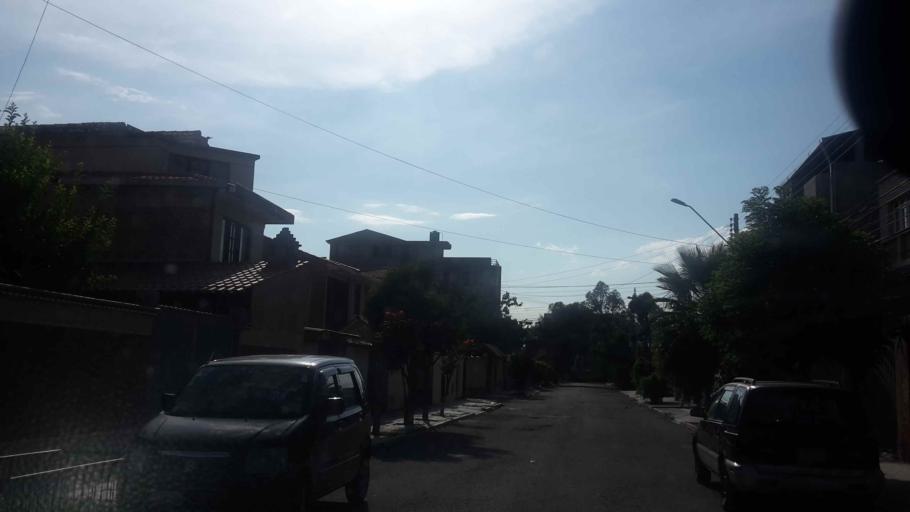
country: BO
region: Cochabamba
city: Cochabamba
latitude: -17.3792
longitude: -66.1943
